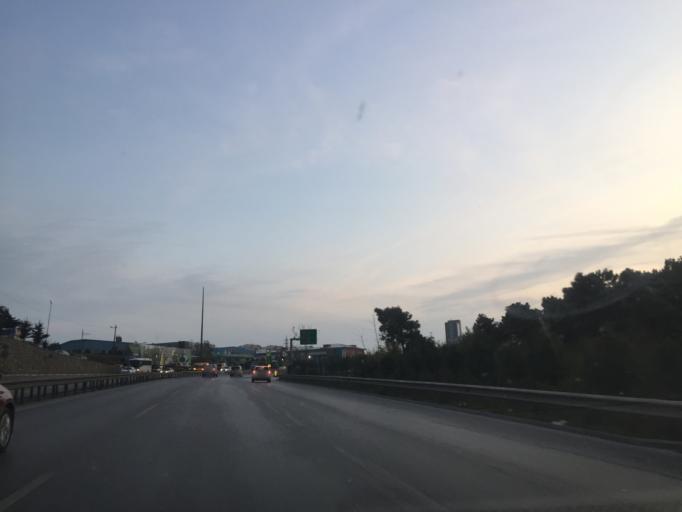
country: TR
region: Istanbul
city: Samandira
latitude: 40.9718
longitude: 29.2195
